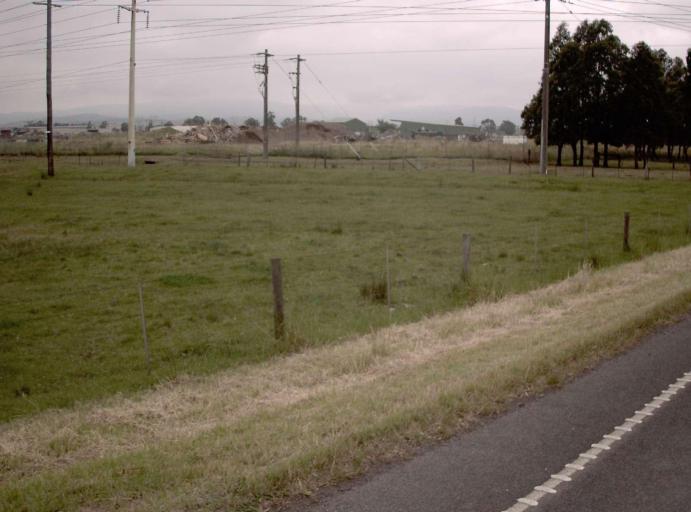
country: AU
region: Victoria
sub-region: Latrobe
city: Morwell
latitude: -38.2533
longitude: 146.4248
